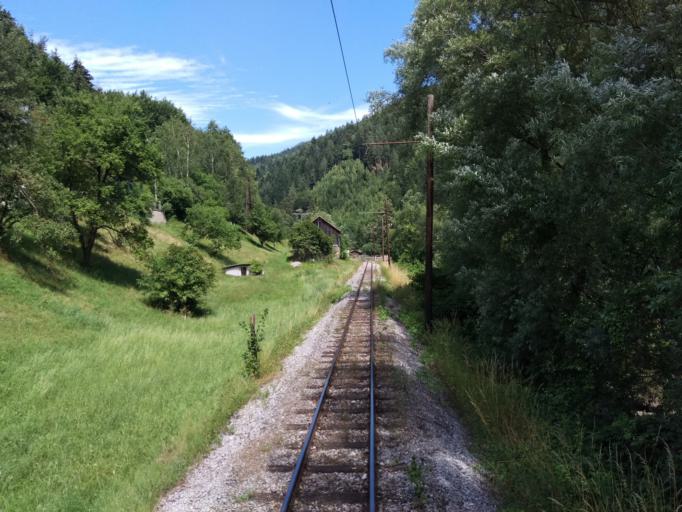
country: AT
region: Styria
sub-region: Politischer Bezirk Bruck-Muerzzuschlag
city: Pernegg an der Mur
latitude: 47.3475
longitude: 15.3621
